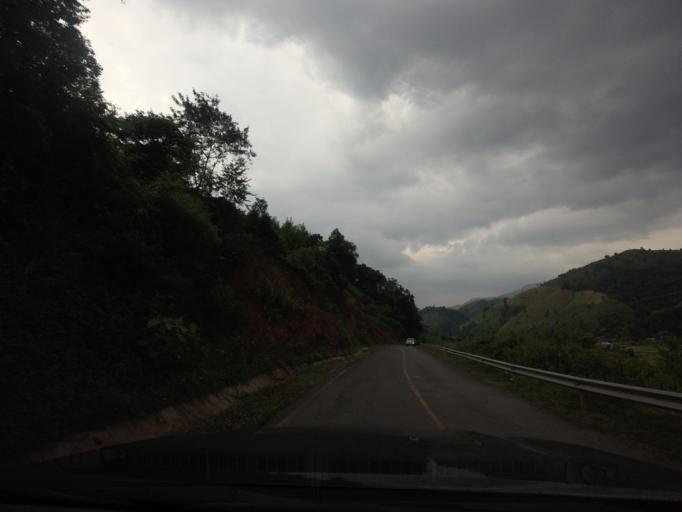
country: TH
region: Nan
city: Bo Kluea
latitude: 19.3488
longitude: 101.1589
